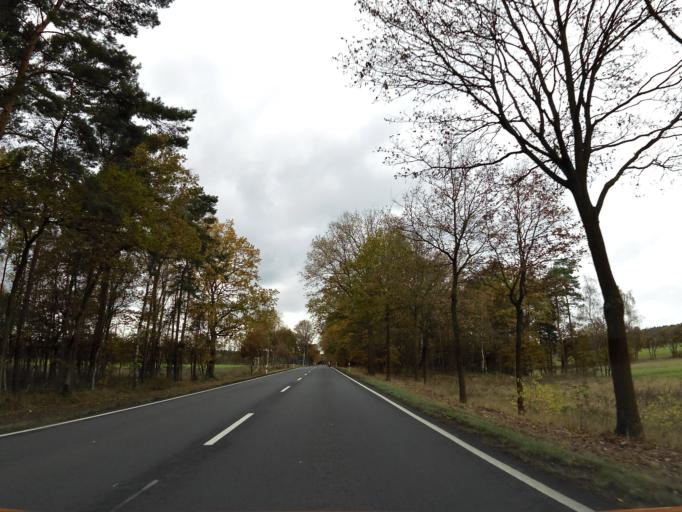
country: DE
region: Lower Saxony
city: Schnega
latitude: 52.9123
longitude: 10.8952
